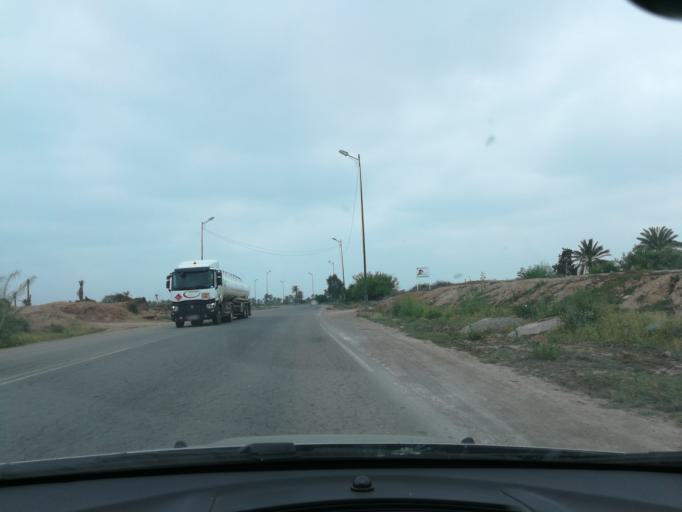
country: MA
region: Marrakech-Tensift-Al Haouz
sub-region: Marrakech
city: Marrakesh
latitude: 31.6892
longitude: -8.0035
